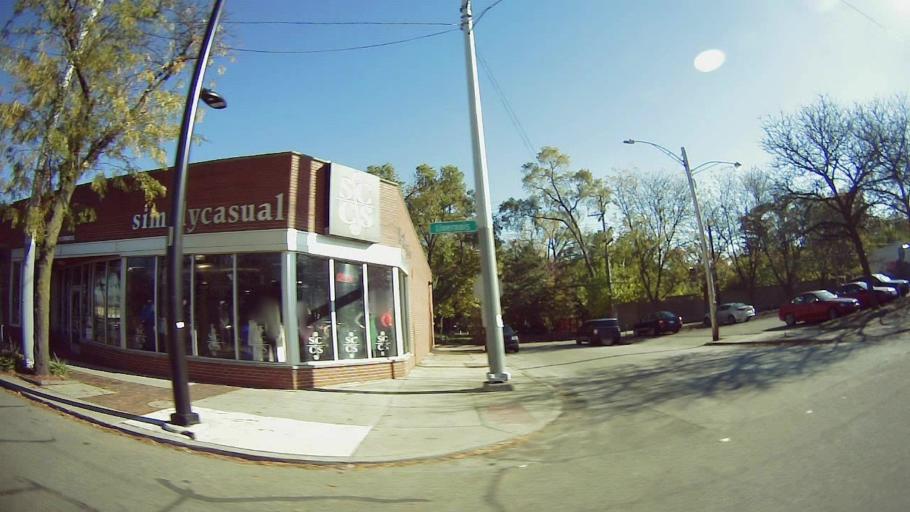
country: US
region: Michigan
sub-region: Oakland County
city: Ferndale
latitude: 42.4361
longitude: -83.1415
